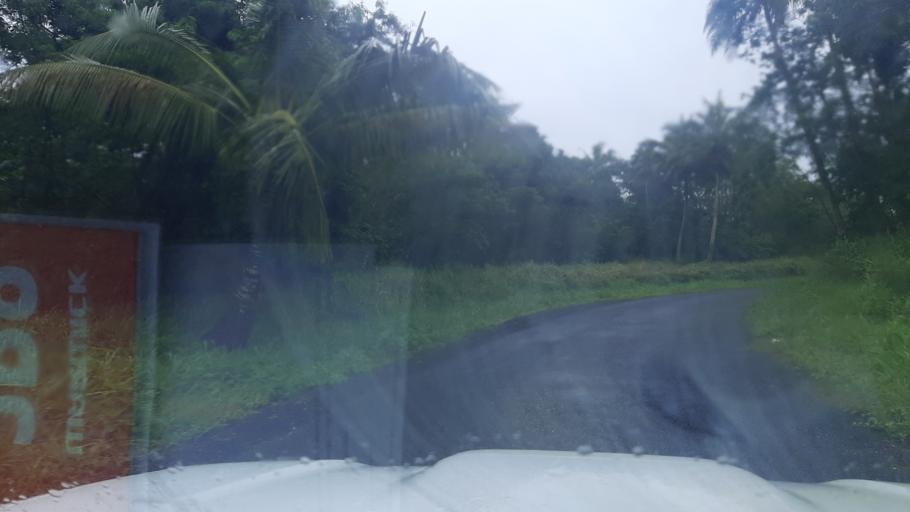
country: VU
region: Shefa
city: Port-Vila
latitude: -17.6401
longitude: 168.2118
